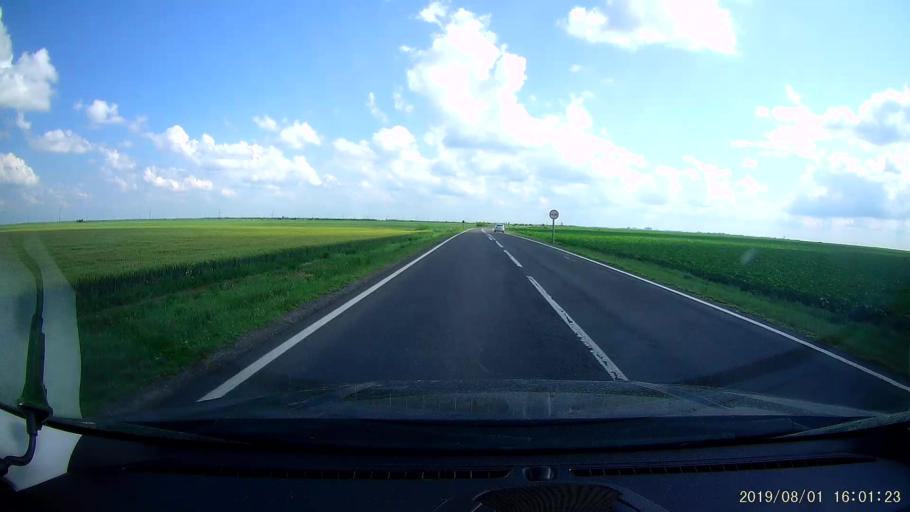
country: RO
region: Ialomita
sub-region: Comuna Ciulnita
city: Ciulnita
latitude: 44.5094
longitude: 27.3902
